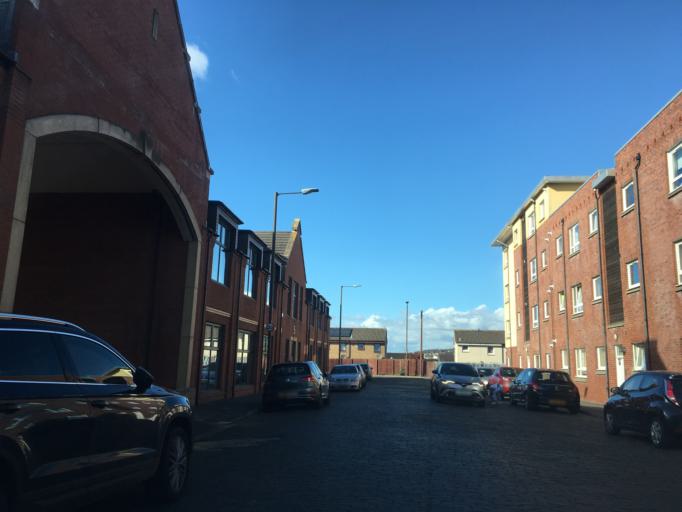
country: GB
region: Scotland
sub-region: Edinburgh
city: Colinton
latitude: 55.9275
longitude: -3.2490
